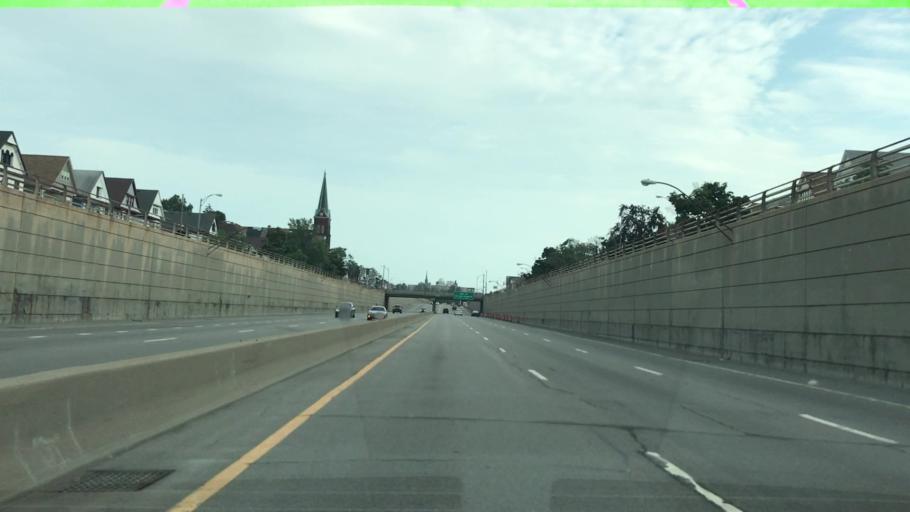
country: US
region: New York
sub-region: Erie County
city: Buffalo
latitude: 42.9136
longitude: -78.8434
